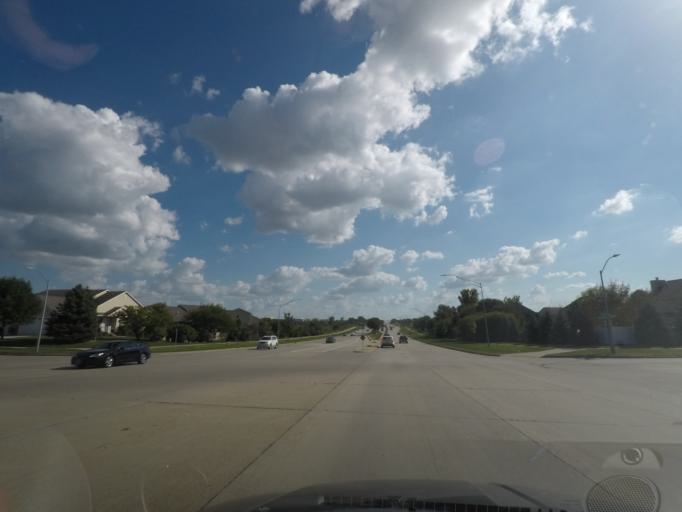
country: US
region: Iowa
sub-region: Dallas County
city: Waukee
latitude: 41.5770
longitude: -93.8093
